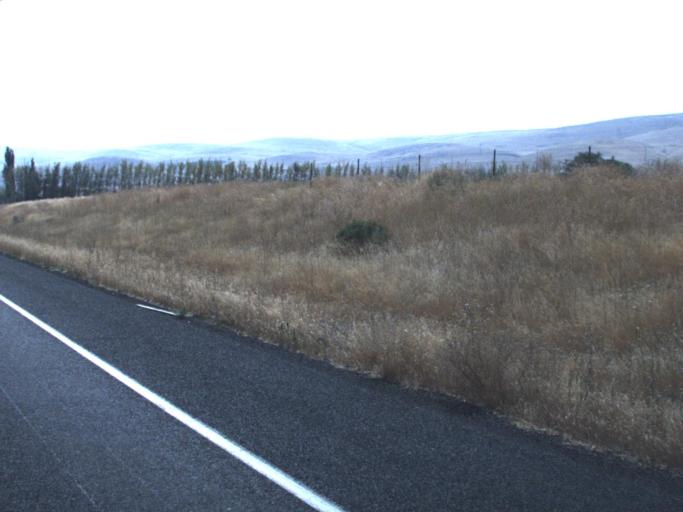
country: US
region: Washington
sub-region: Yakima County
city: Zillah
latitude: 46.5082
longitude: -120.1926
